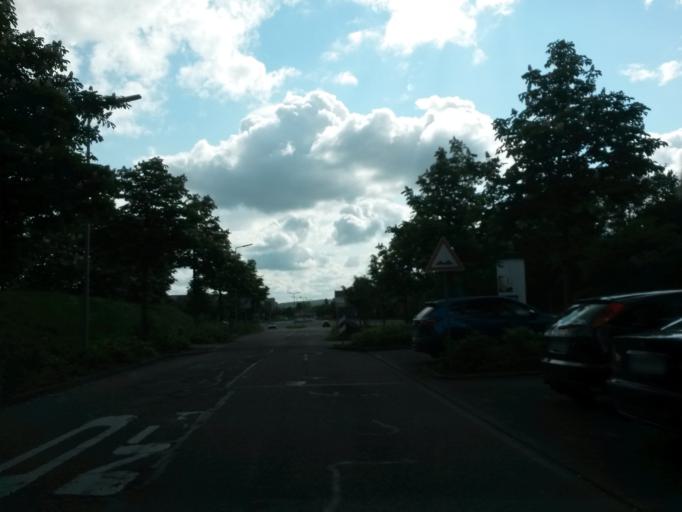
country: DE
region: Baden-Wuerttemberg
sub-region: Karlsruhe Region
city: Karlsruhe
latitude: 49.0348
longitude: 8.4489
